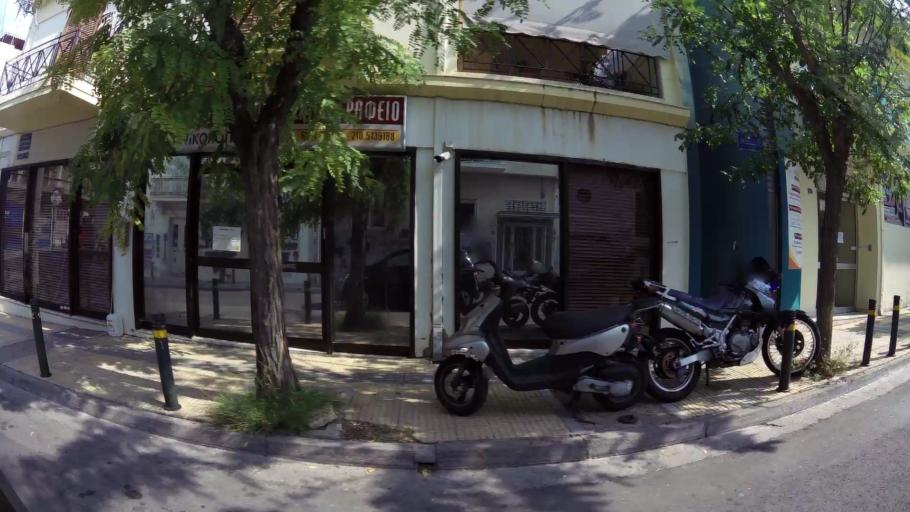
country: GR
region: Attica
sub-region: Nomarchia Athinas
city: Athens
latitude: 37.9967
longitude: 23.7159
